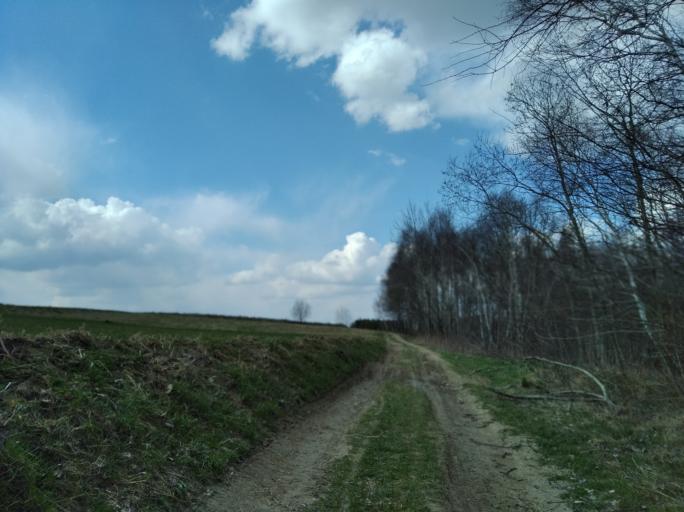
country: PL
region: Subcarpathian Voivodeship
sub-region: Powiat strzyzowski
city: Strzyzow
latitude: 49.9104
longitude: 21.7536
